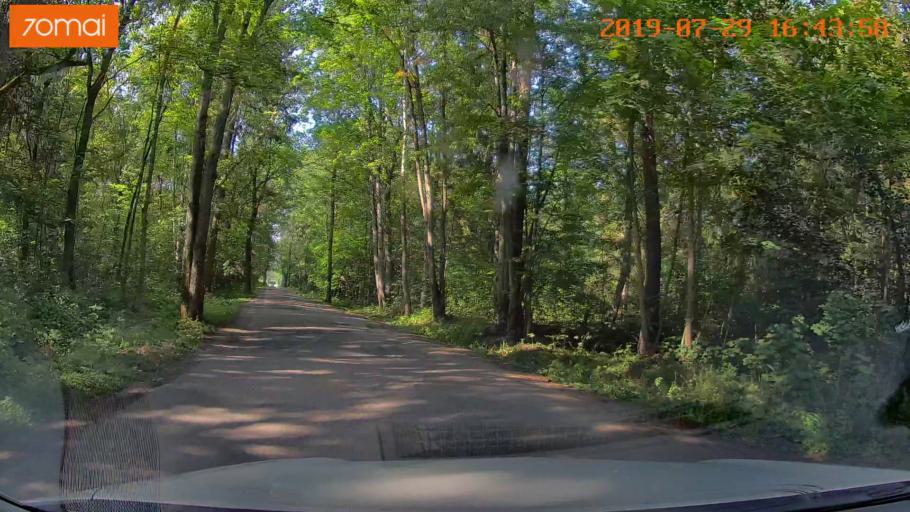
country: RU
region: Kaliningrad
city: Primorsk
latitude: 54.7520
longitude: 20.0901
